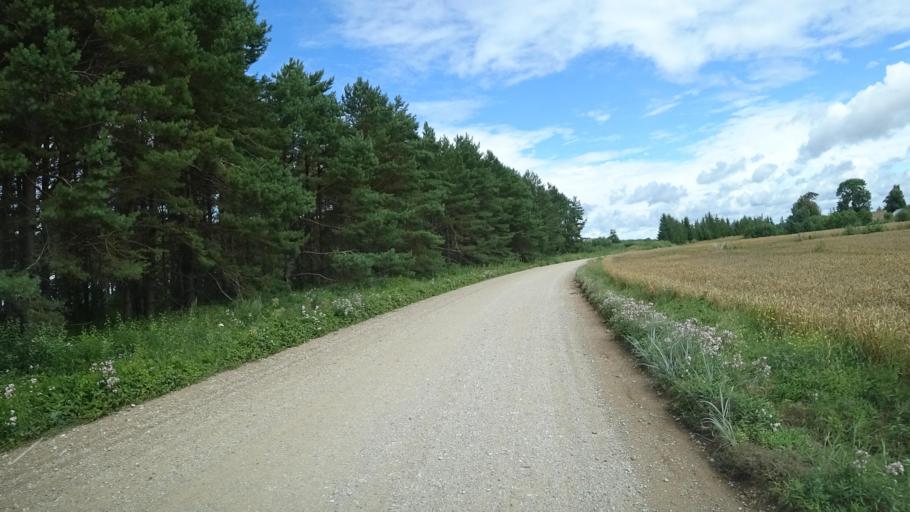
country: LV
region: Liepaja
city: Vec-Liepaja
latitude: 56.6475
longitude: 21.0446
